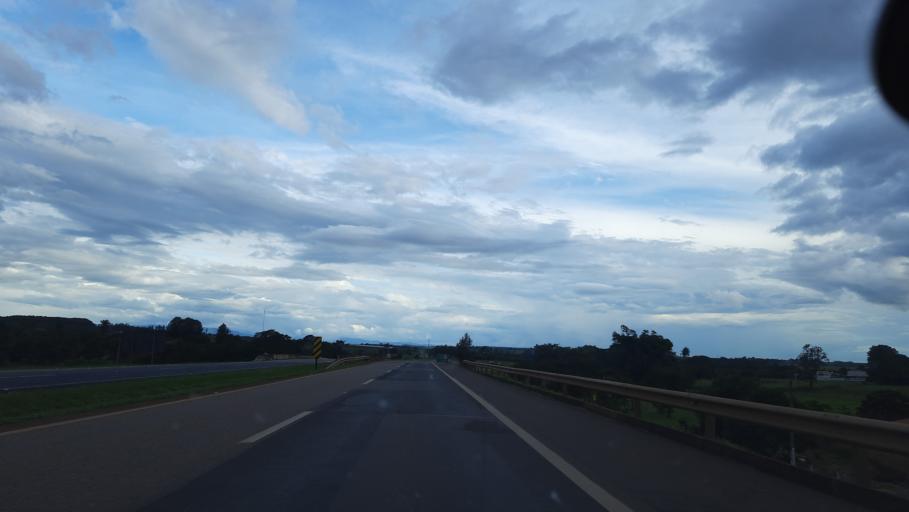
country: BR
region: Sao Paulo
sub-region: Casa Branca
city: Casa Branca
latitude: -21.7710
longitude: -47.0650
